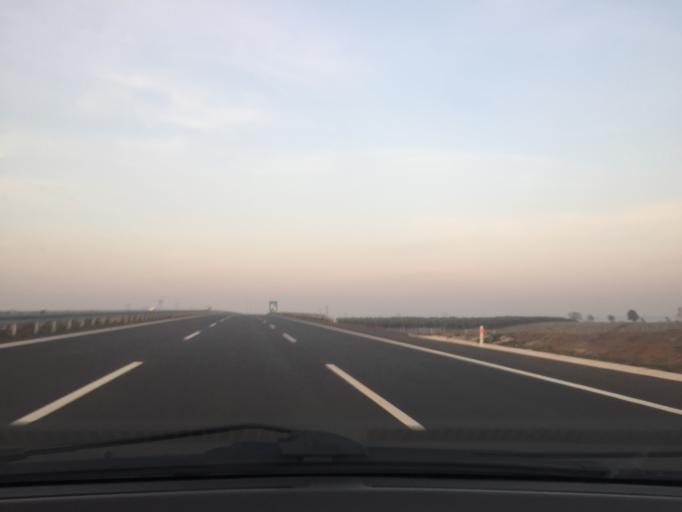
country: TR
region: Bursa
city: Mahmudiye
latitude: 40.2706
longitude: 28.6197
